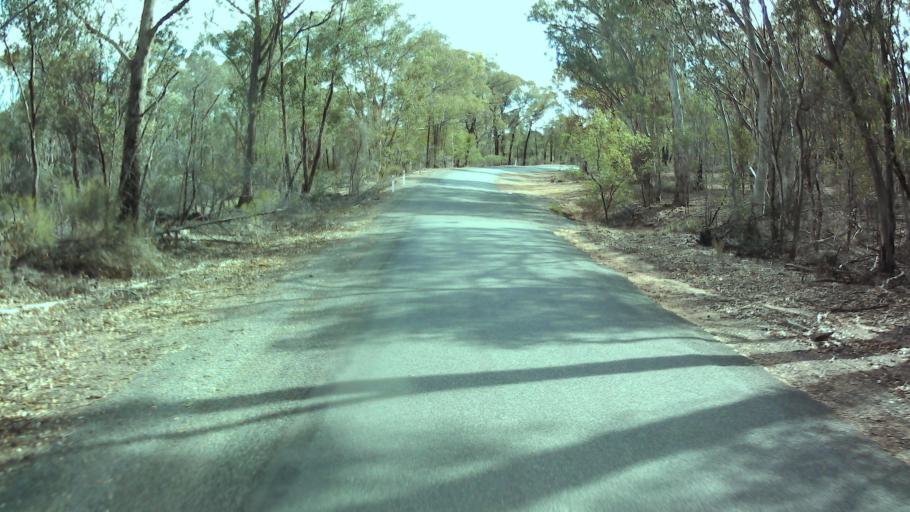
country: AU
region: New South Wales
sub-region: Weddin
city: Grenfell
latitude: -33.8660
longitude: 148.2068
